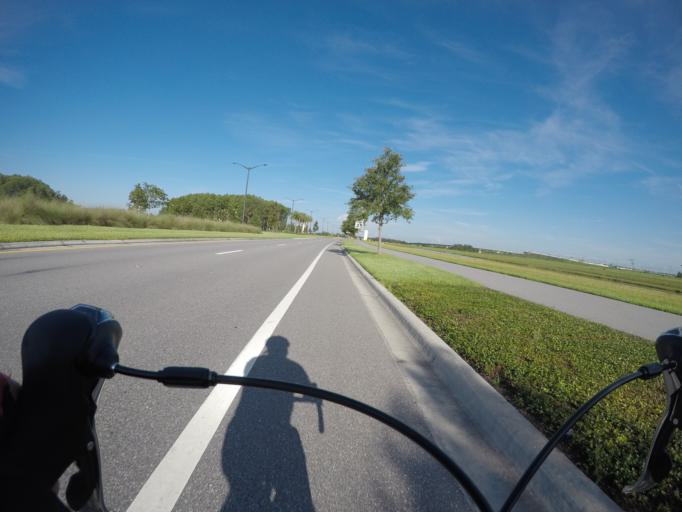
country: US
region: Florida
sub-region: Osceola County
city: Buenaventura Lakes
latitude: 28.3651
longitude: -81.2996
